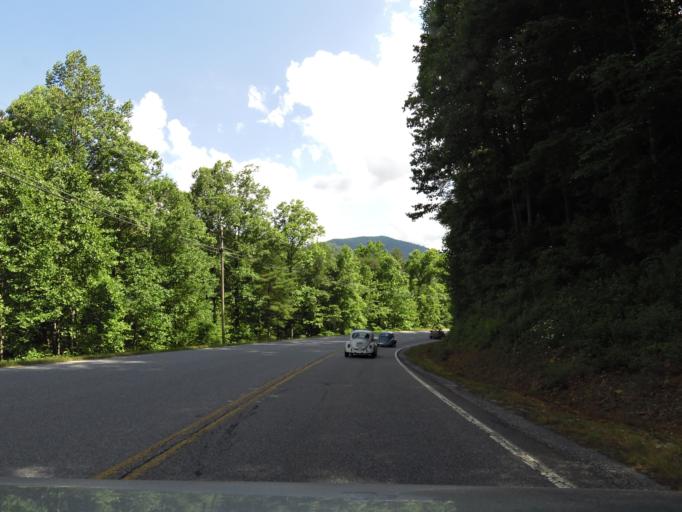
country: US
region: Georgia
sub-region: Towns County
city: Hiawassee
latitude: 34.8362
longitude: -83.7281
